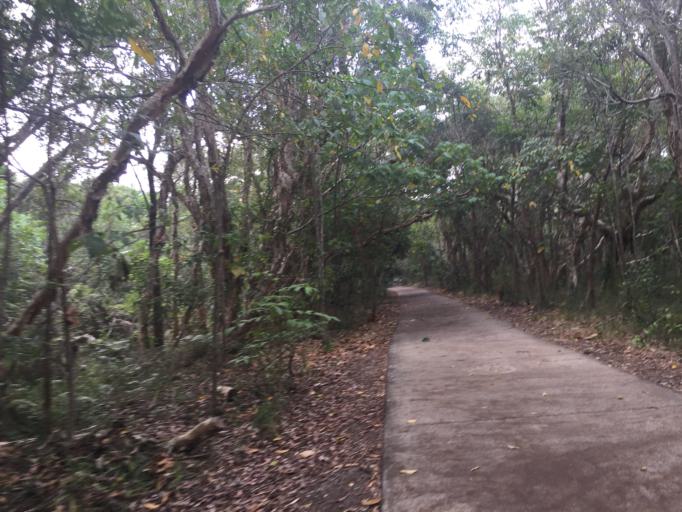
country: AU
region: Queensland
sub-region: Sunshine Coast
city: Coolum Beach
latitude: -26.5725
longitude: 153.0972
